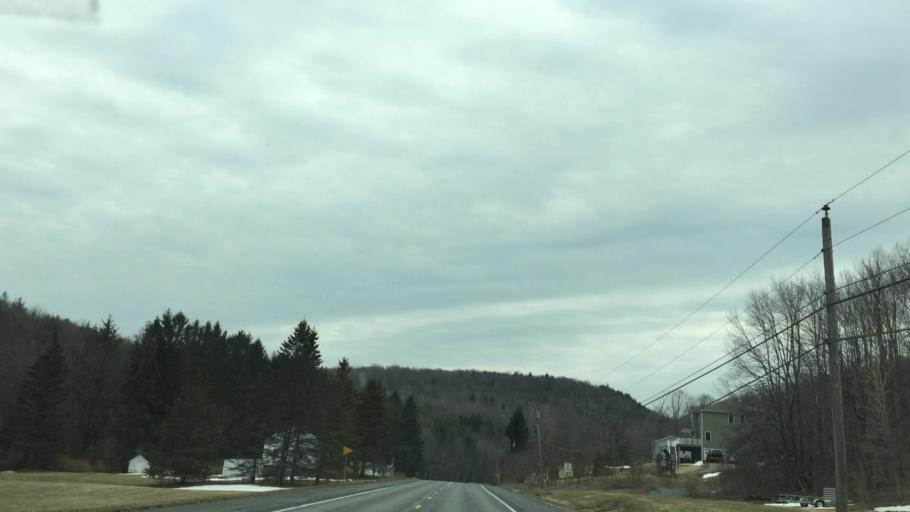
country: US
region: Massachusetts
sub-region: Berkshire County
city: Williamstown
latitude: 42.6214
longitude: -73.2305
